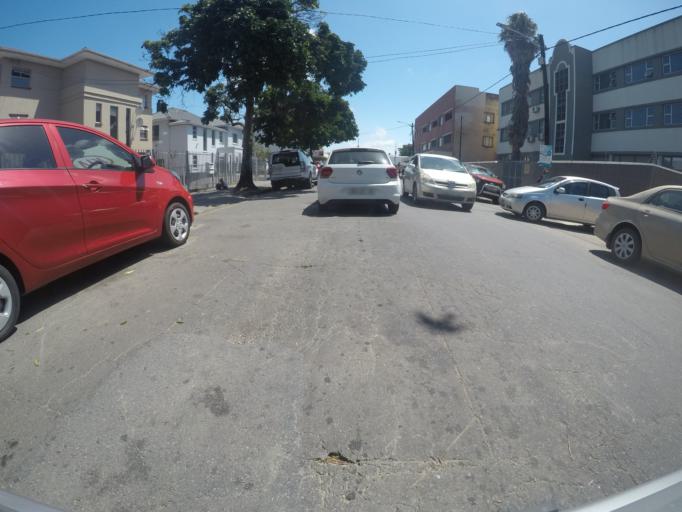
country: ZA
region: Eastern Cape
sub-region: Buffalo City Metropolitan Municipality
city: East London
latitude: -33.0053
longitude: 27.9014
